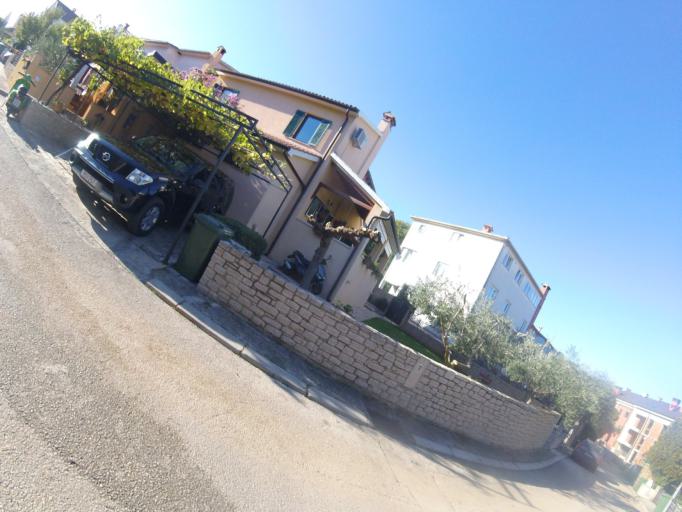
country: HR
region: Istarska
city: Vrsar
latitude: 45.1536
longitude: 13.6108
